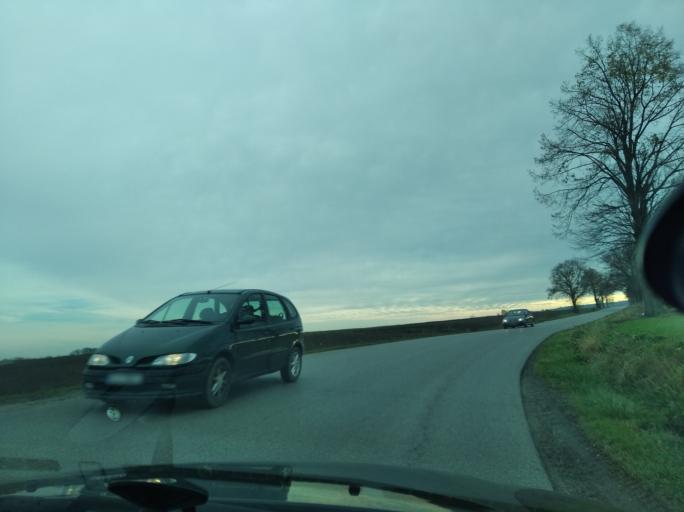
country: PL
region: Subcarpathian Voivodeship
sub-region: Powiat lancucki
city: Wysoka
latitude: 50.0236
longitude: 22.2591
